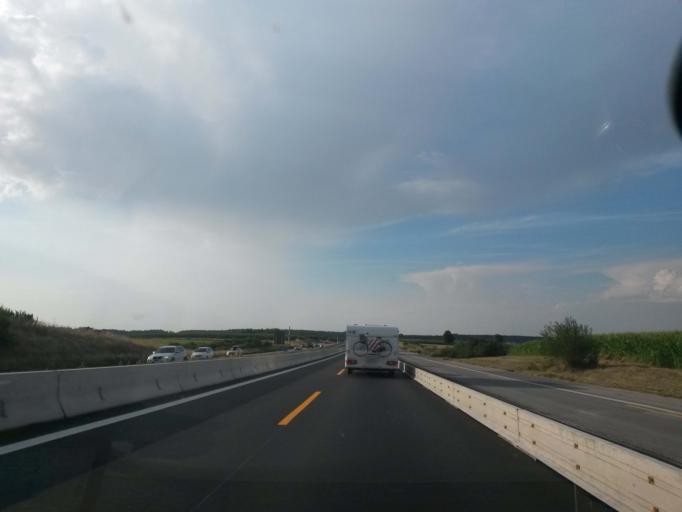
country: DE
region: Bavaria
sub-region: Upper Bavaria
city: Schweitenkirchen
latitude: 48.5395
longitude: 11.5950
